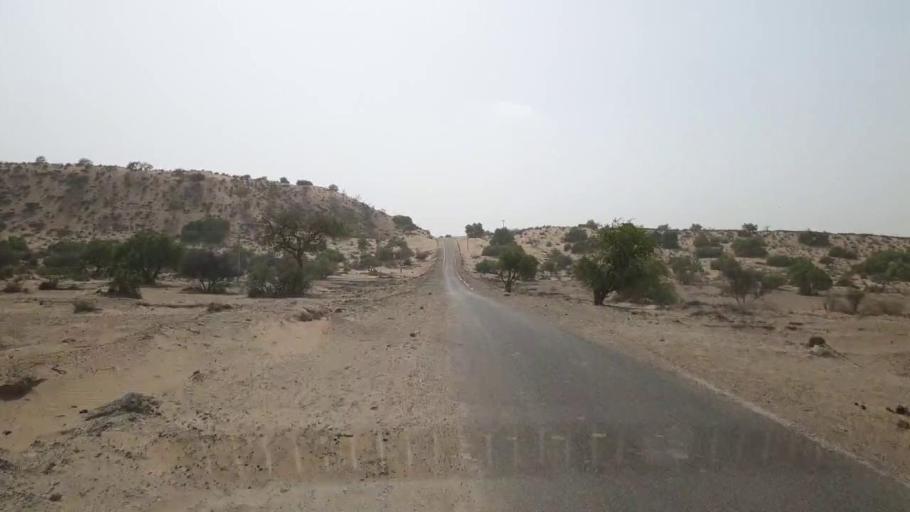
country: PK
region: Sindh
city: Mithi
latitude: 24.6205
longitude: 69.9152
